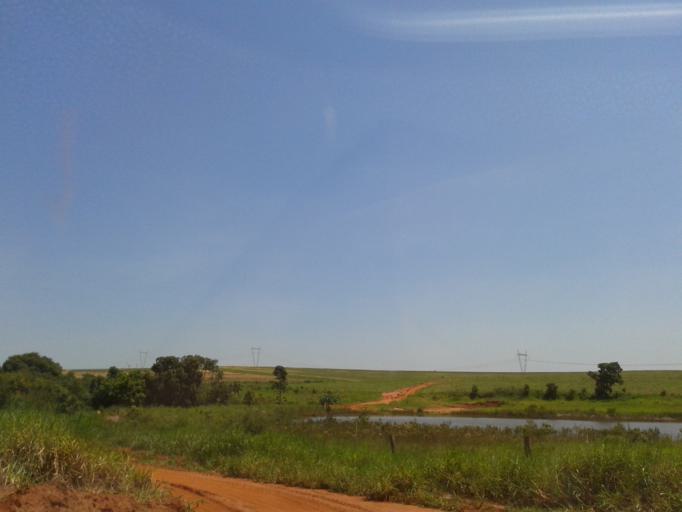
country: BR
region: Minas Gerais
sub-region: Santa Vitoria
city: Santa Vitoria
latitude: -19.0974
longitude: -50.4539
